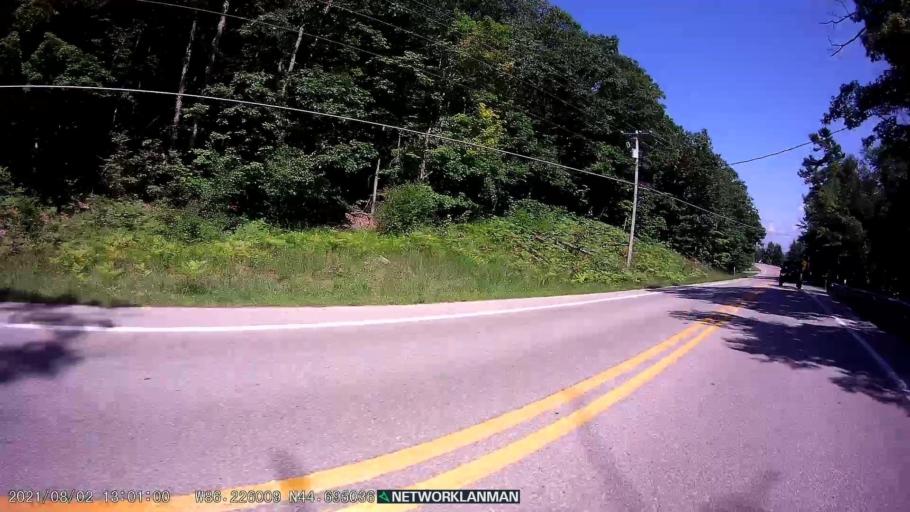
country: US
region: Michigan
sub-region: Benzie County
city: Frankfort
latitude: 44.6948
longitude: -86.2257
